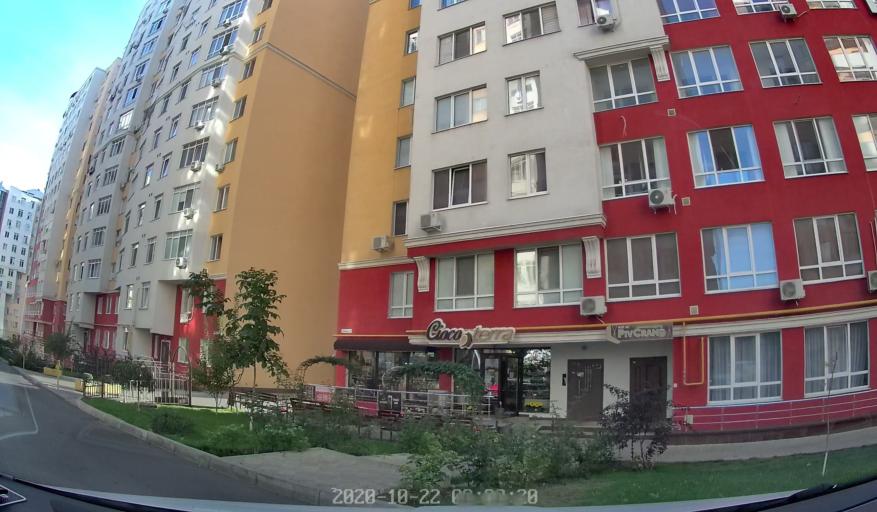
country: MD
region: Chisinau
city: Chisinau
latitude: 46.9965
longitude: 28.8345
